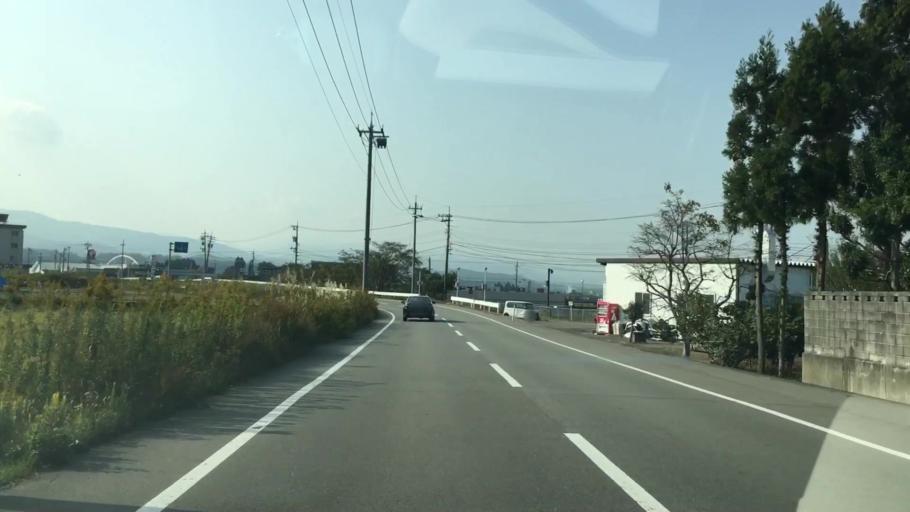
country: JP
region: Toyama
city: Toyama-shi
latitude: 36.6201
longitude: 137.2885
